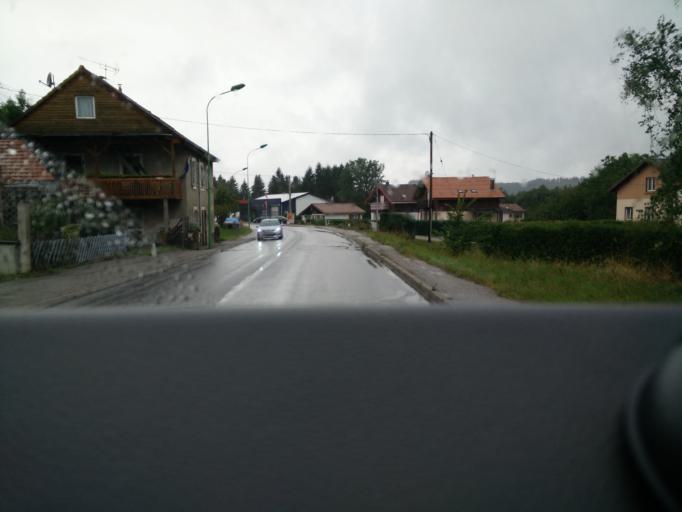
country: FR
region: Lorraine
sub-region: Departement des Vosges
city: Fraize
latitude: 48.1848
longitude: 6.9944
